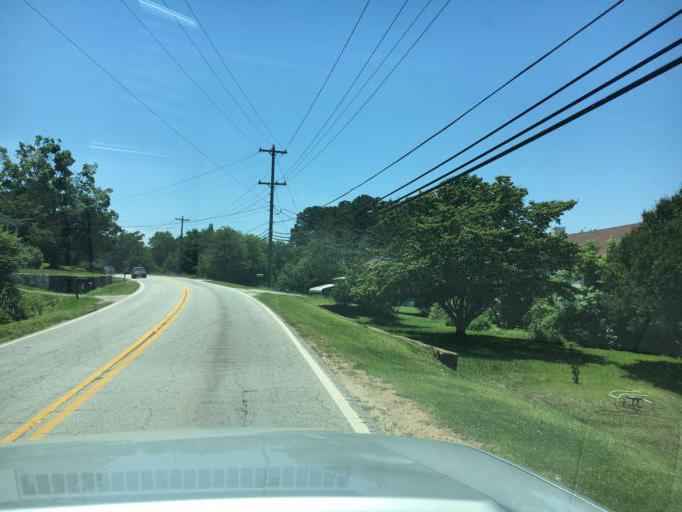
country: US
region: South Carolina
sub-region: Greenville County
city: Greer
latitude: 34.9529
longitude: -82.2120
